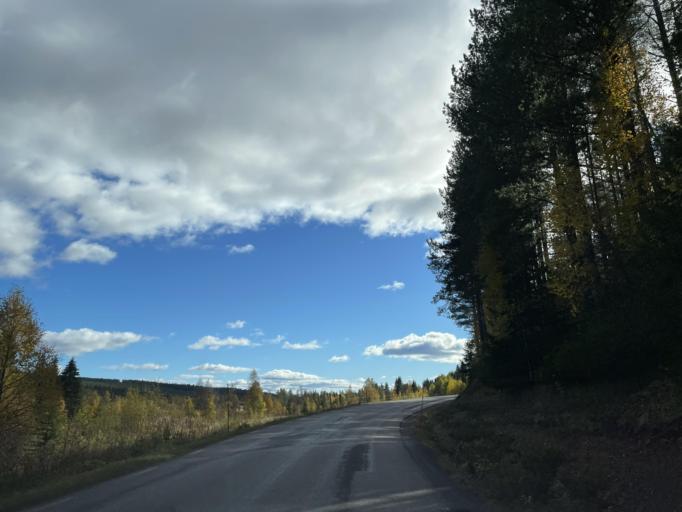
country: SE
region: Dalarna
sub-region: Malung-Saelens kommun
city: Malung
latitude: 61.1376
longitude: 13.2723
